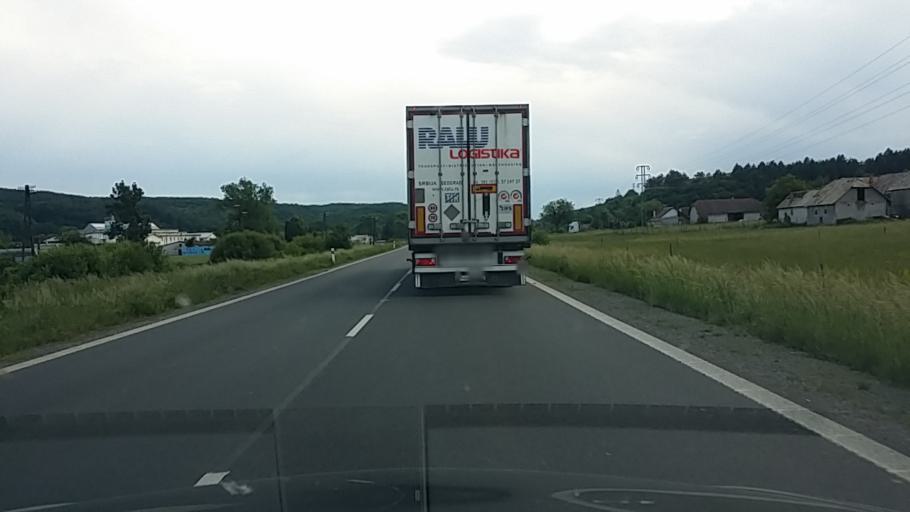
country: SK
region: Banskobystricky
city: Krupina
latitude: 48.3300
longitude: 19.0607
